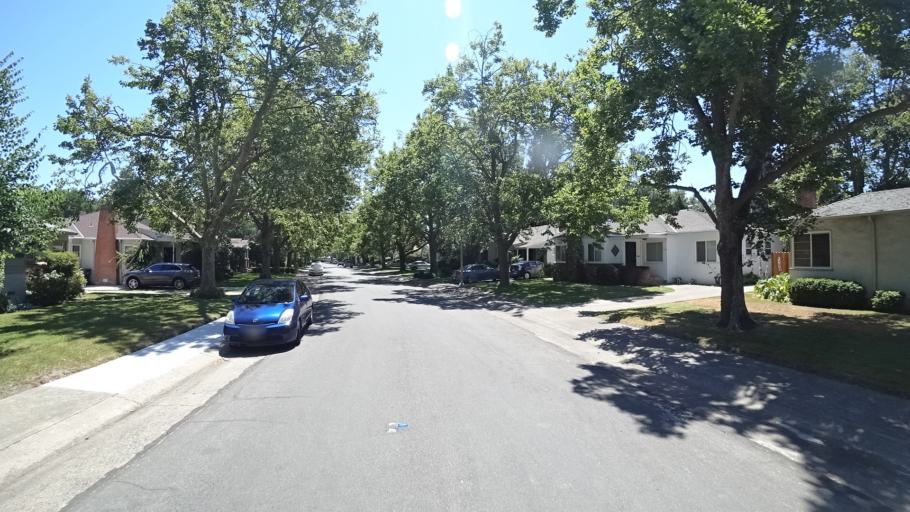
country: US
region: California
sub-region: Sacramento County
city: Sacramento
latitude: 38.5446
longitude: -121.5071
